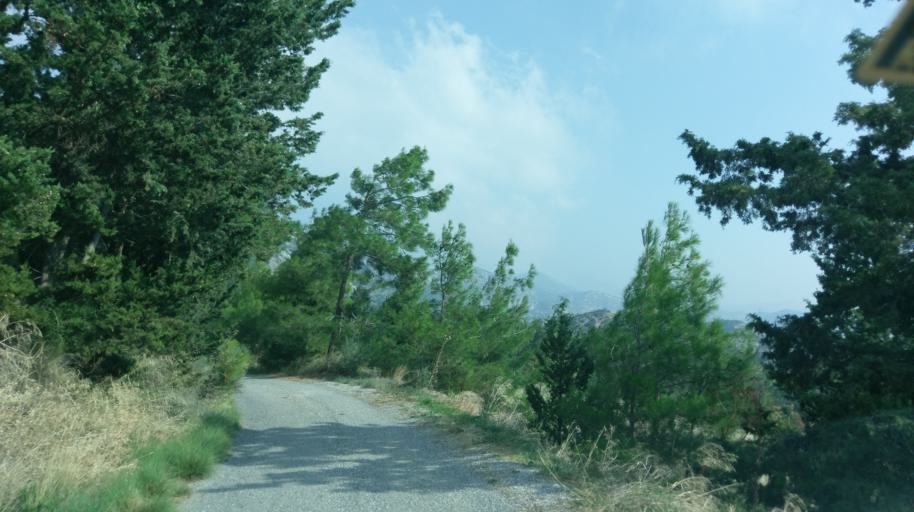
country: CY
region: Ammochostos
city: Lefkonoiko
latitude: 35.3161
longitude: 33.6202
